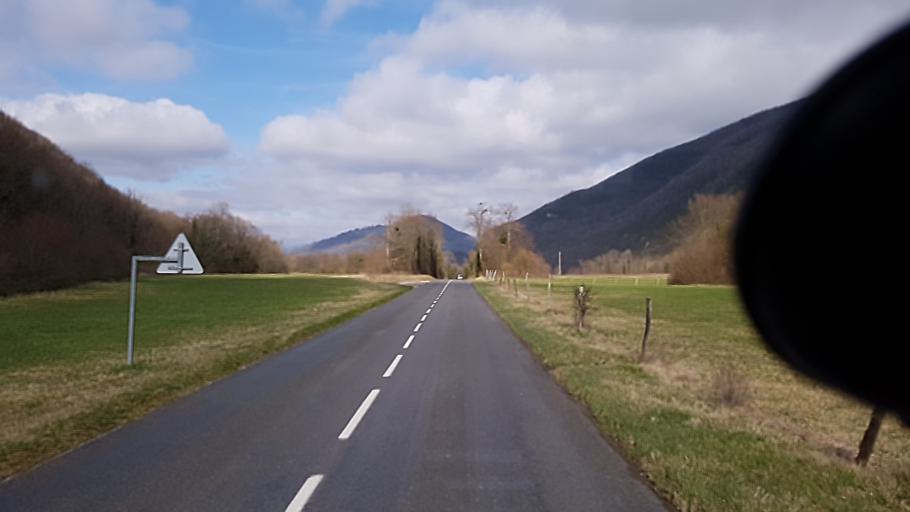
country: FR
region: Rhone-Alpes
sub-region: Departement de l'Ain
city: Izernore
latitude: 46.2499
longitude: 5.5017
